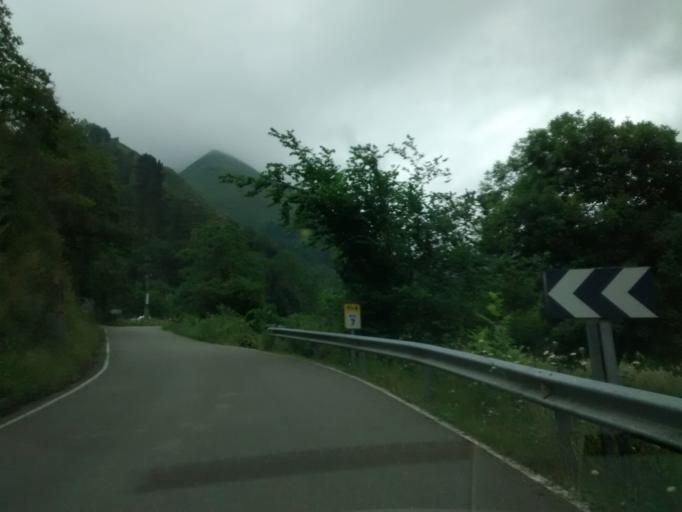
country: ES
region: Asturias
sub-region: Province of Asturias
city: Pilona
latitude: 43.2895
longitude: -5.3559
